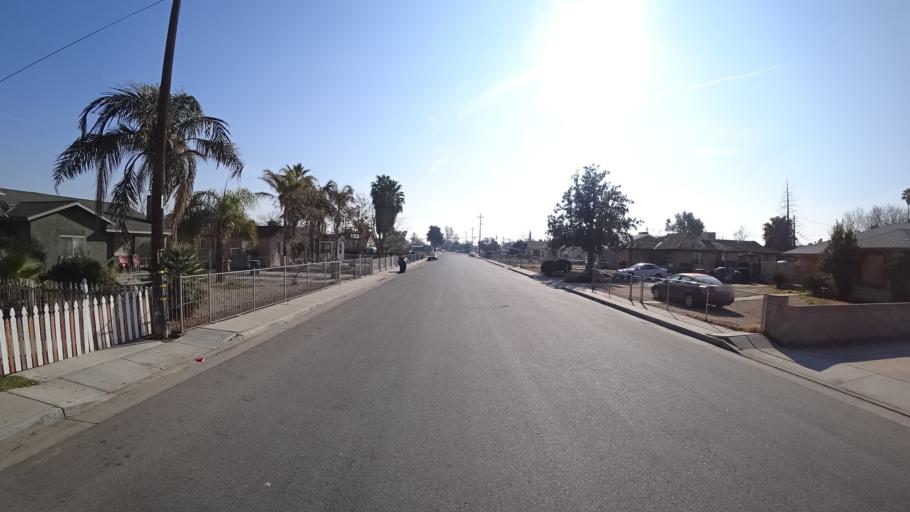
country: US
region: California
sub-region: Kern County
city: Bakersfield
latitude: 35.3620
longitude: -119.0052
